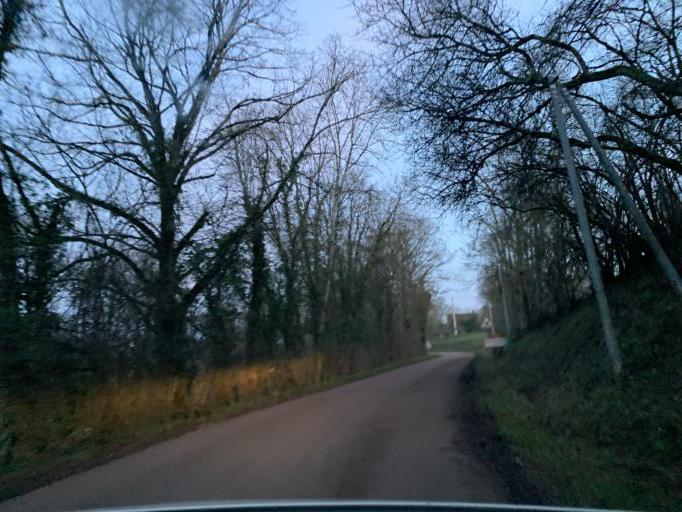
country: FR
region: Bourgogne
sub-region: Departement de l'Yonne
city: Fontenailles
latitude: 47.5659
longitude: 3.3404
